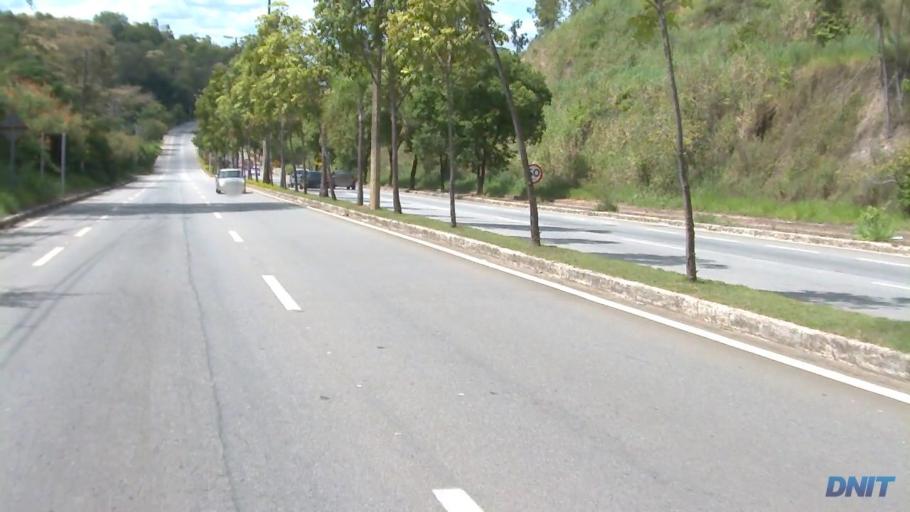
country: BR
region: Minas Gerais
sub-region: Coronel Fabriciano
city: Coronel Fabriciano
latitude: -19.5080
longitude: -42.5835
